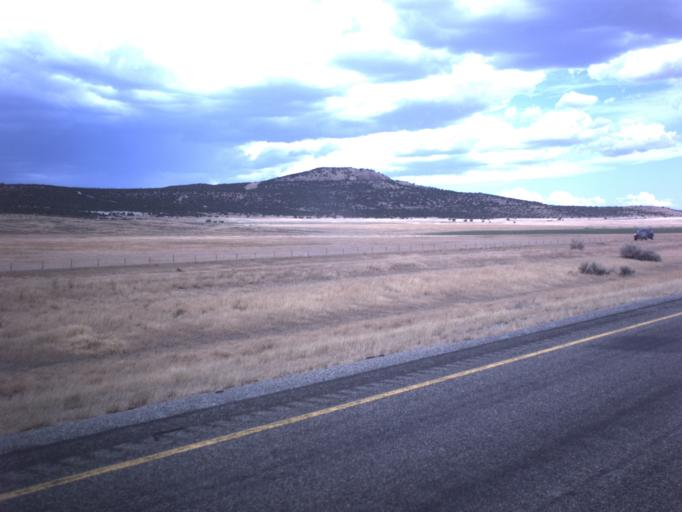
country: US
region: Idaho
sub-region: Oneida County
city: Malad City
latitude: 41.9840
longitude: -112.8101
